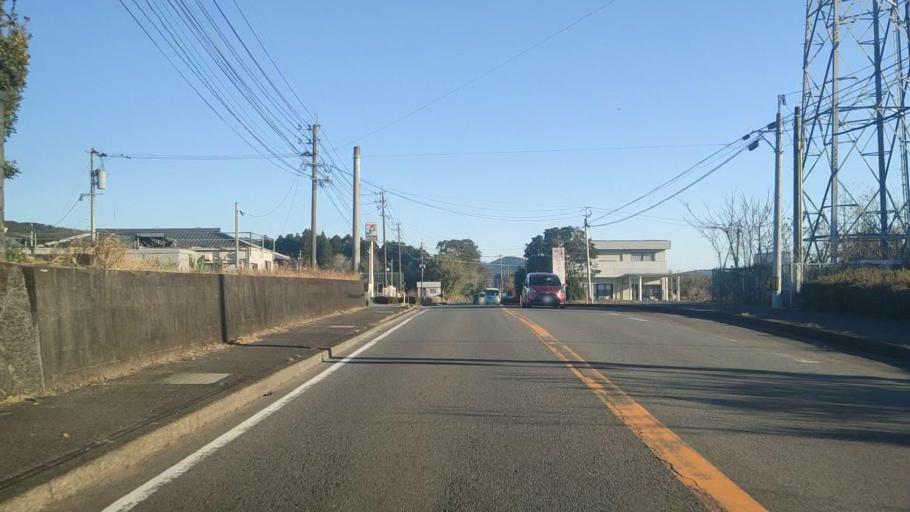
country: JP
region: Miyazaki
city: Takanabe
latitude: 32.3036
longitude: 131.5819
